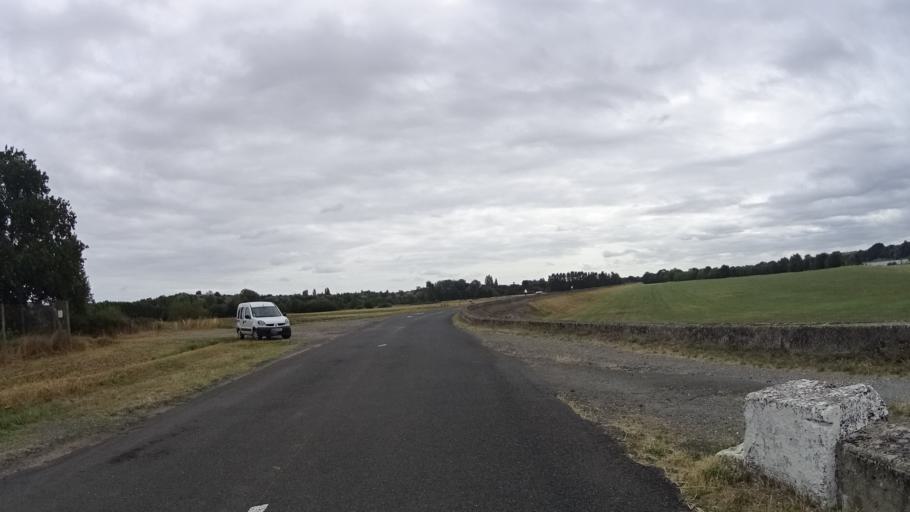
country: FR
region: Pays de la Loire
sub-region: Departement de Maine-et-Loire
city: La Possonniere
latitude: 47.3648
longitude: -0.7172
